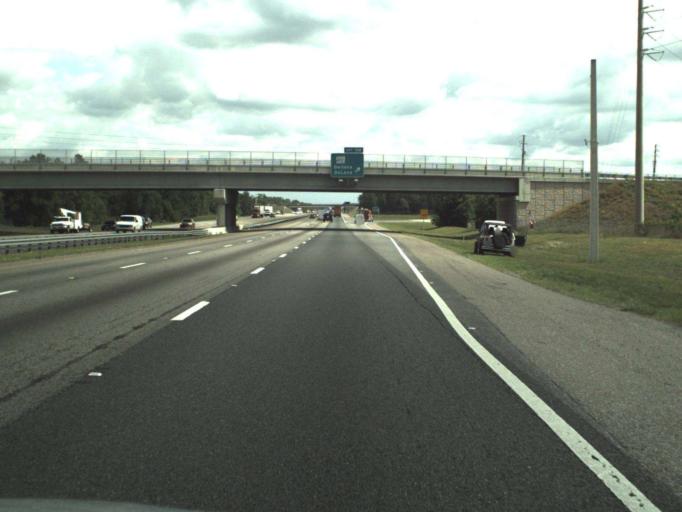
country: US
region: Florida
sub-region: Volusia County
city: Orange City
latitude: 28.9475
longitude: -81.2600
